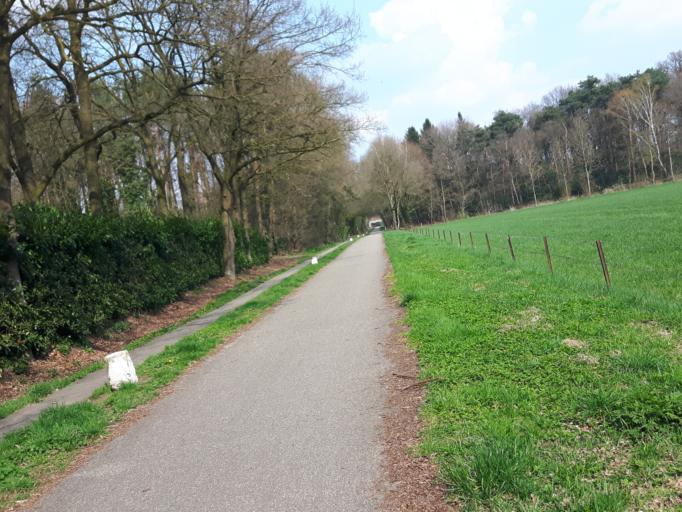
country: NL
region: Overijssel
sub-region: Gemeente Enschede
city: Enschede
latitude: 52.1862
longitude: 6.8447
